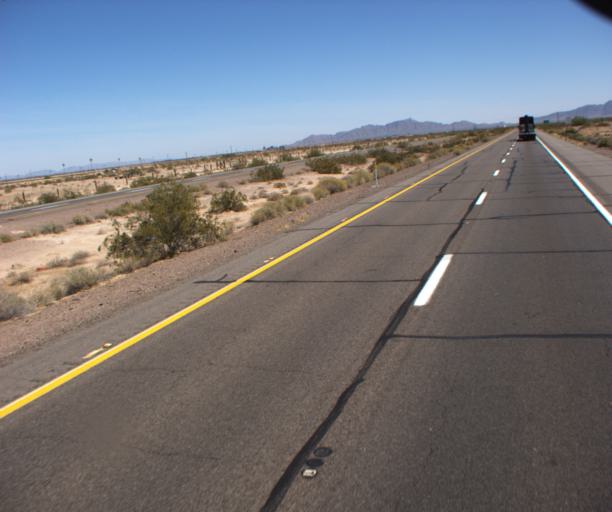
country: US
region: Arizona
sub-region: Yuma County
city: Wellton
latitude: 32.6951
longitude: -113.9420
